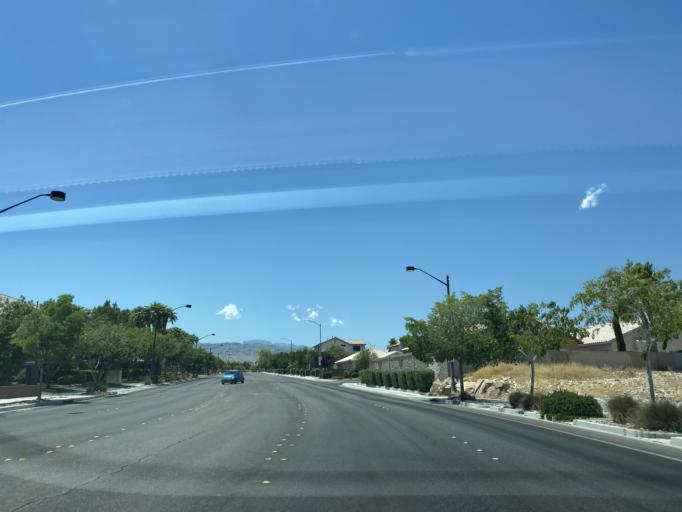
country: US
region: Nevada
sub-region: Clark County
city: Las Vegas
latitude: 36.2842
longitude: -115.2645
